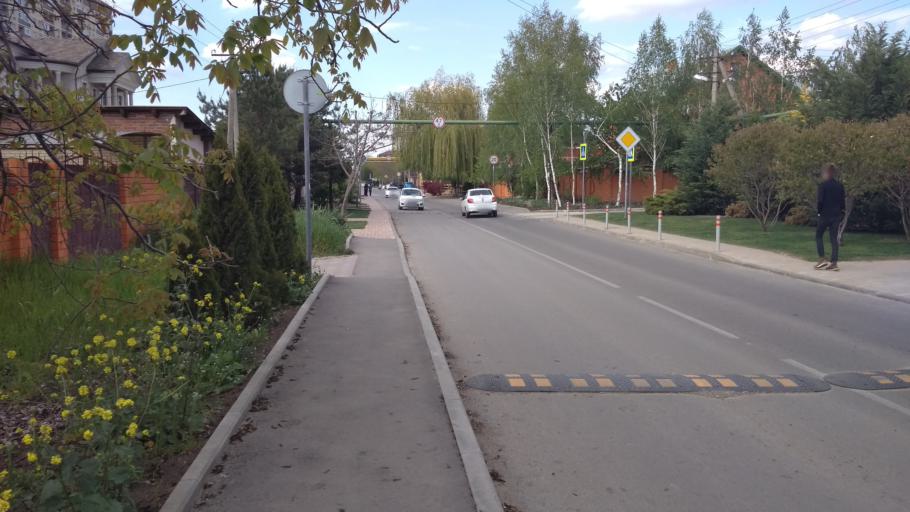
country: RU
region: Krasnodarskiy
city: Krasnodar
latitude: 45.0762
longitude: 39.0048
